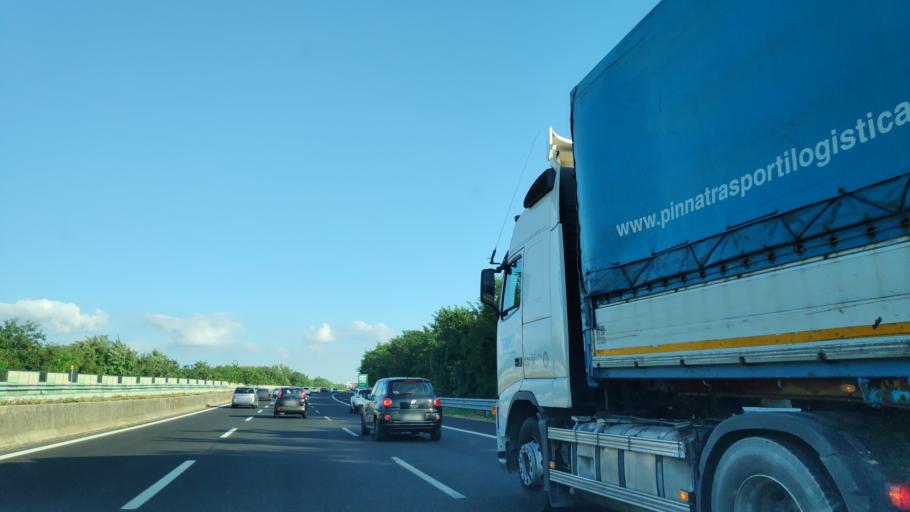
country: IT
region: Campania
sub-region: Provincia di Caserta
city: Casagiove
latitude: 41.0723
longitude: 14.3025
